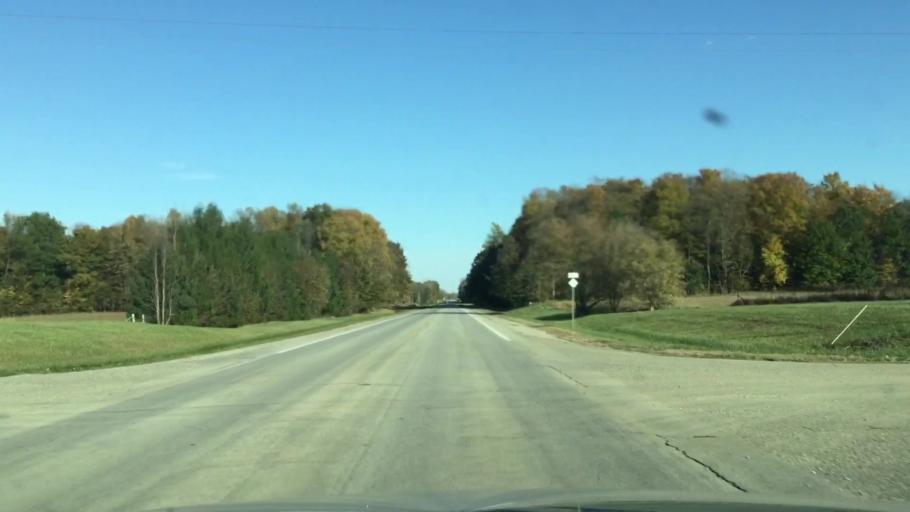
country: US
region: Michigan
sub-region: Lapeer County
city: Barnes Lake-Millers Lake
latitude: 43.2277
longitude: -83.2744
